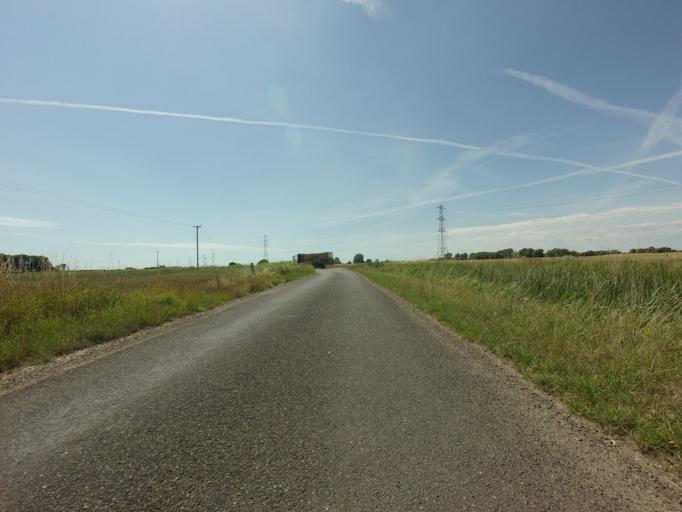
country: GB
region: England
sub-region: Kent
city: Lydd
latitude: 50.9713
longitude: 0.8970
